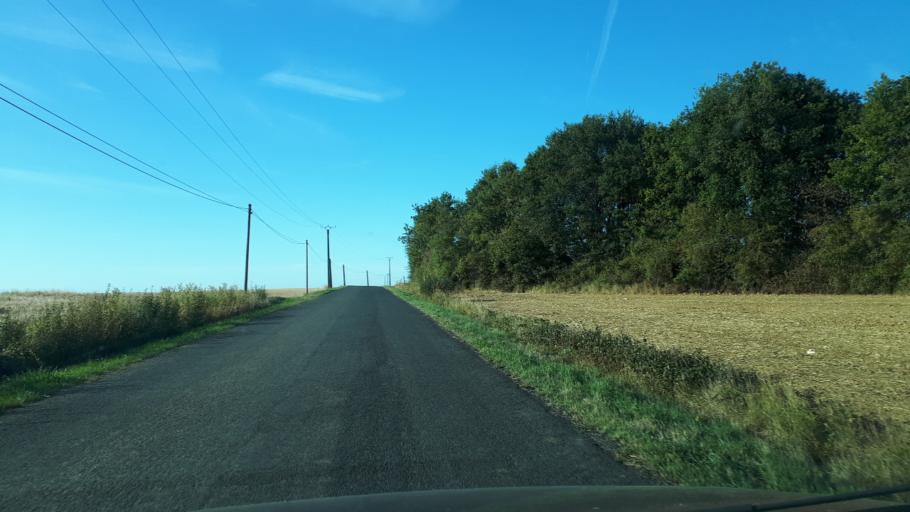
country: FR
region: Centre
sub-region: Departement du Loir-et-Cher
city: Lunay
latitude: 47.7401
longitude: 0.9362
